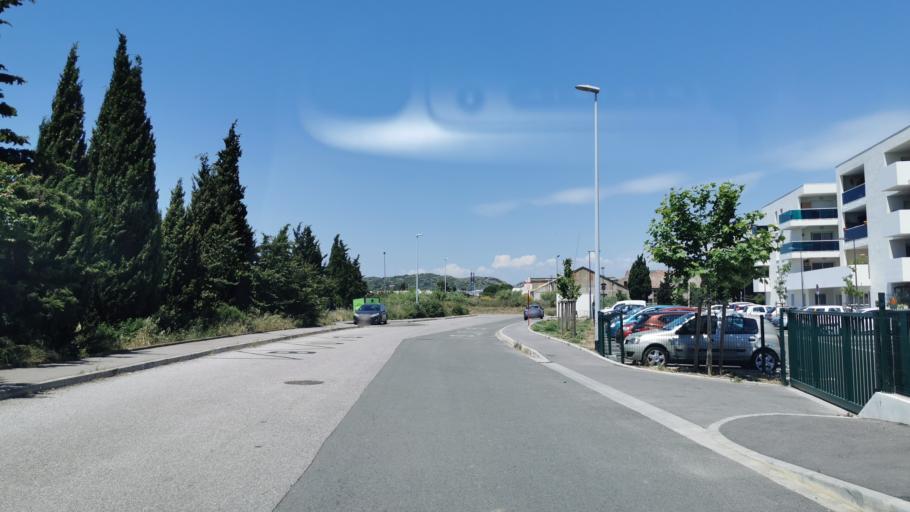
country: FR
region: Languedoc-Roussillon
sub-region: Departement de l'Aude
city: Narbonne
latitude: 43.1676
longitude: 2.9924
